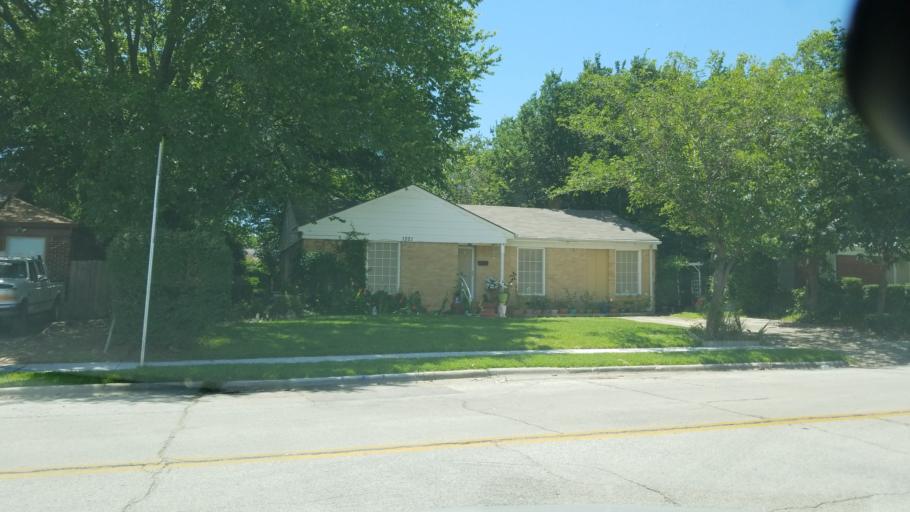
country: US
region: Texas
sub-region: Dallas County
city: Irving
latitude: 32.8300
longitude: -96.9697
